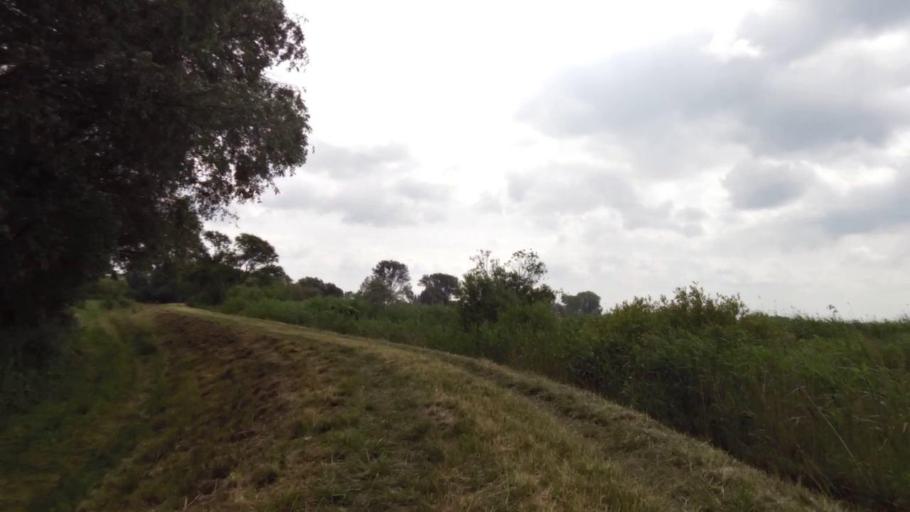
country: PL
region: West Pomeranian Voivodeship
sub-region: Powiat policki
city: Police
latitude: 53.5092
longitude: 14.6957
